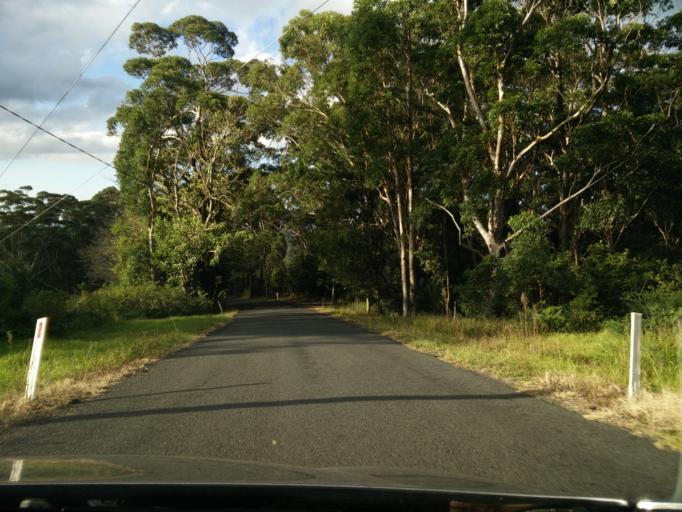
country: AU
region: New South Wales
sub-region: Kiama
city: Jamberoo
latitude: -34.6813
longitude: 150.7904
